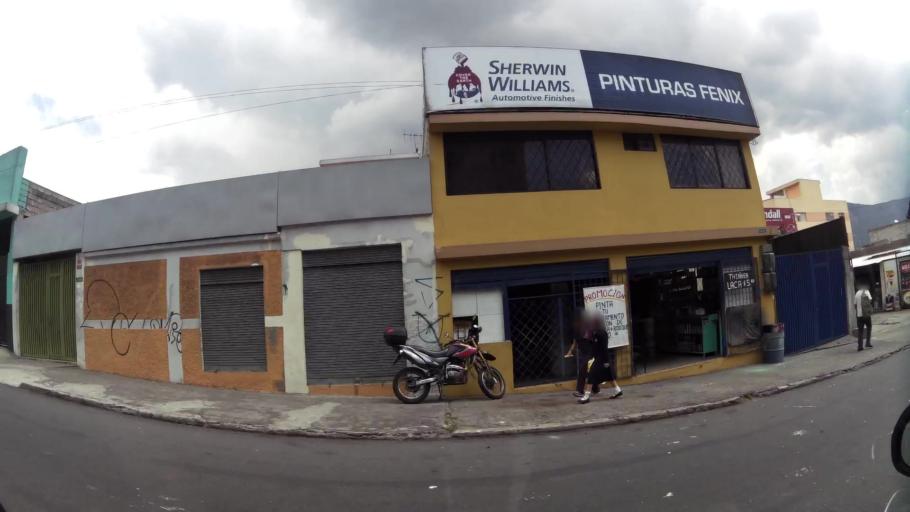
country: EC
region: Pichincha
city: Quito
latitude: -0.2520
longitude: -78.5162
